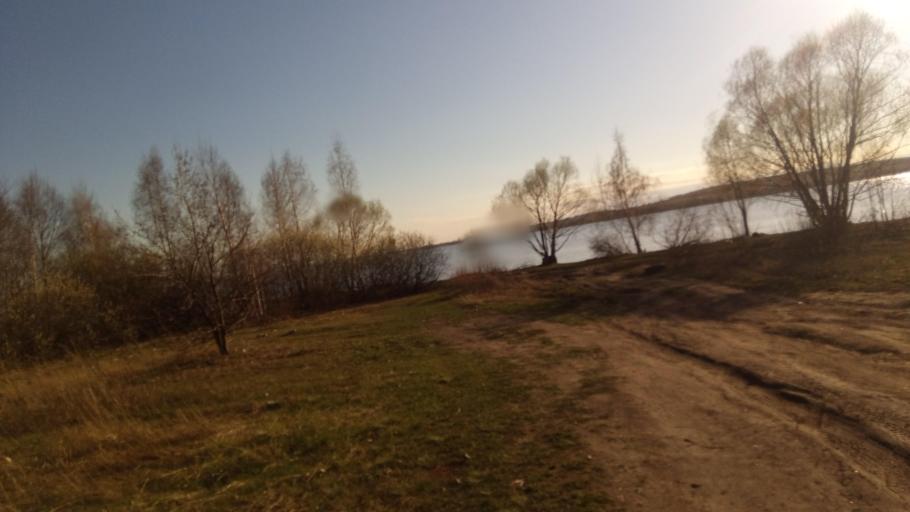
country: RU
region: Chelyabinsk
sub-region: Gorod Chelyabinsk
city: Chelyabinsk
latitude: 55.1340
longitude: 61.3278
